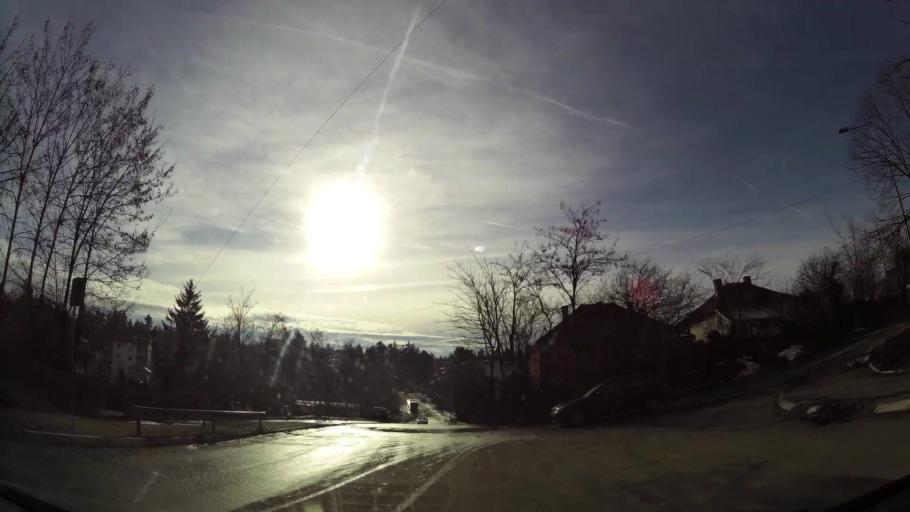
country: RS
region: Central Serbia
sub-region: Belgrade
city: Rakovica
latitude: 44.7226
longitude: 20.4291
